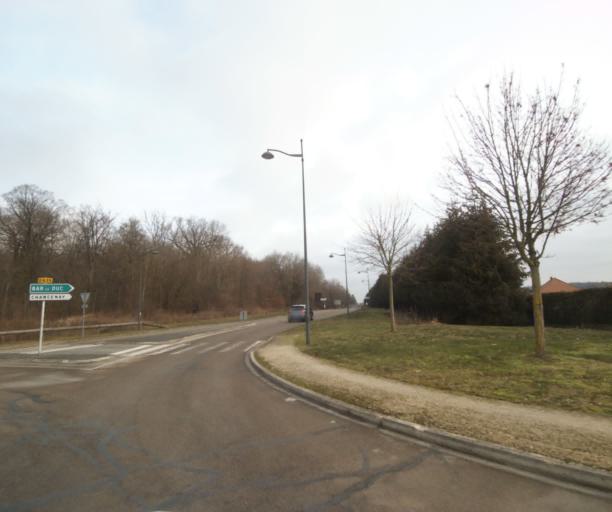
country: FR
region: Champagne-Ardenne
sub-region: Departement de la Haute-Marne
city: Bettancourt-la-Ferree
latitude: 48.6567
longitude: 4.9688
